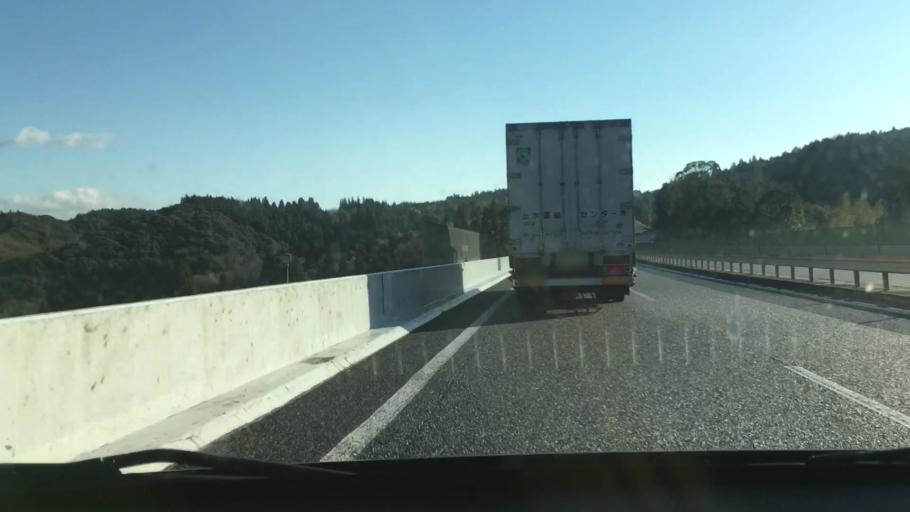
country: JP
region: Kagoshima
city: Kajiki
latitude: 31.8788
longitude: 130.6953
